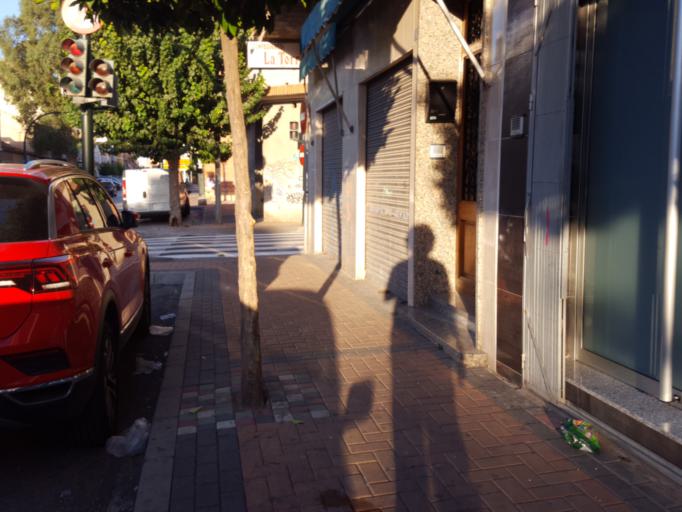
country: ES
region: Murcia
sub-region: Murcia
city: Murcia
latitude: 38.0074
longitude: -1.1600
